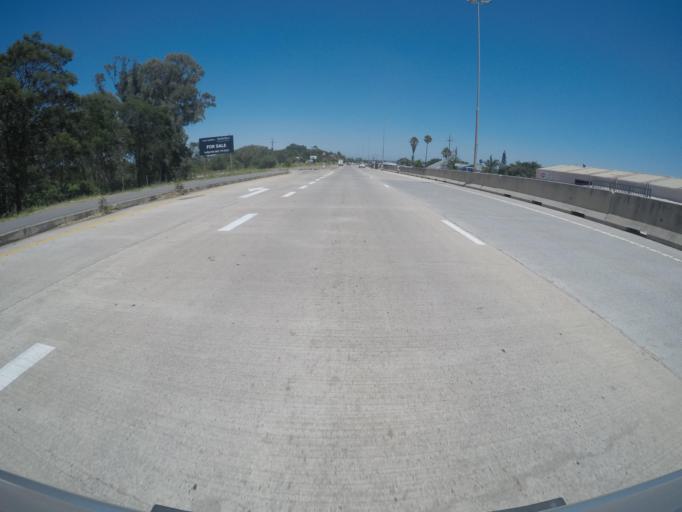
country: ZA
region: Eastern Cape
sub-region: Buffalo City Metropolitan Municipality
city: East London
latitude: -32.9408
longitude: 27.9741
